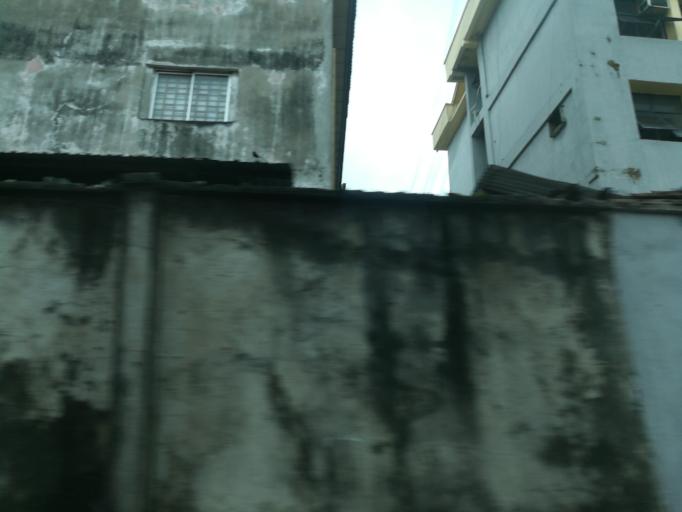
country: NG
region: Rivers
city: Port Harcourt
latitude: 4.8421
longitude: 7.0360
